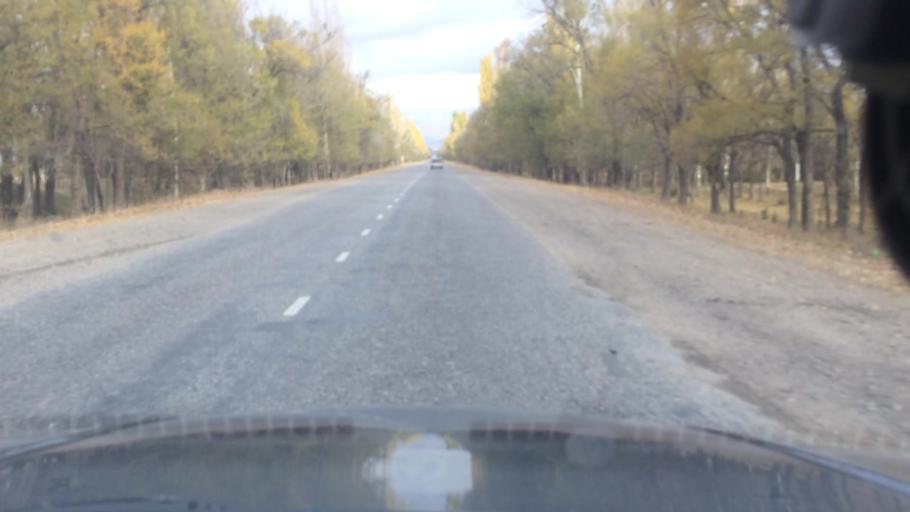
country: KG
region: Ysyk-Koel
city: Tyup
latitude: 42.6313
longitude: 78.3604
